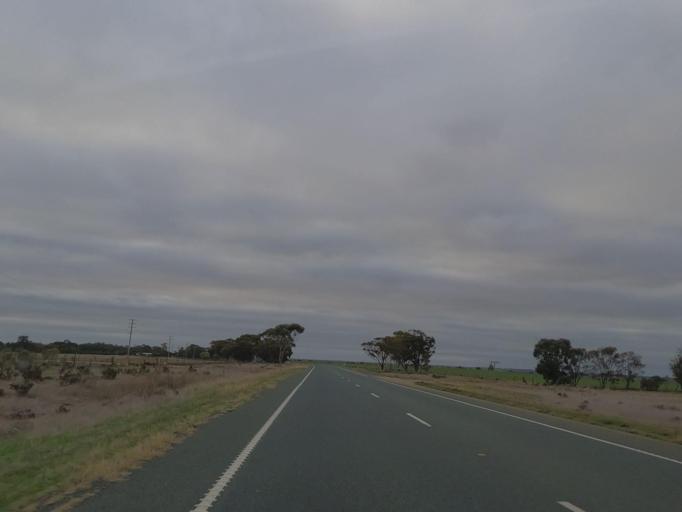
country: AU
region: Victoria
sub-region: Swan Hill
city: Swan Hill
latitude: -35.5649
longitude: 143.7835
